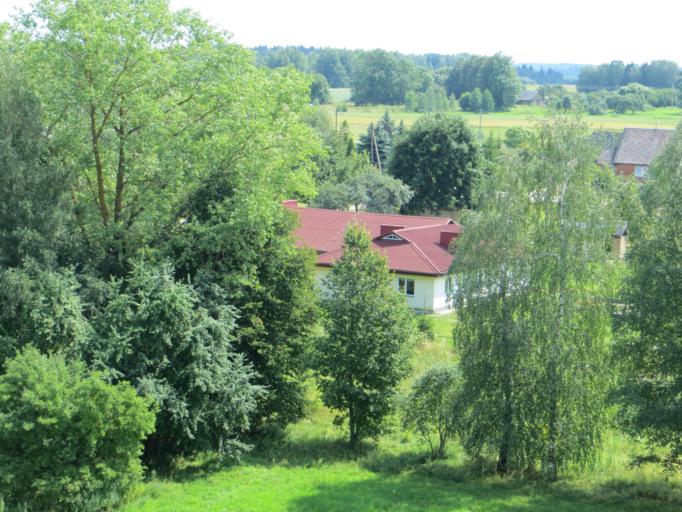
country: LT
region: Vilnius County
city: Ukmerge
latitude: 55.1105
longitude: 24.6916
